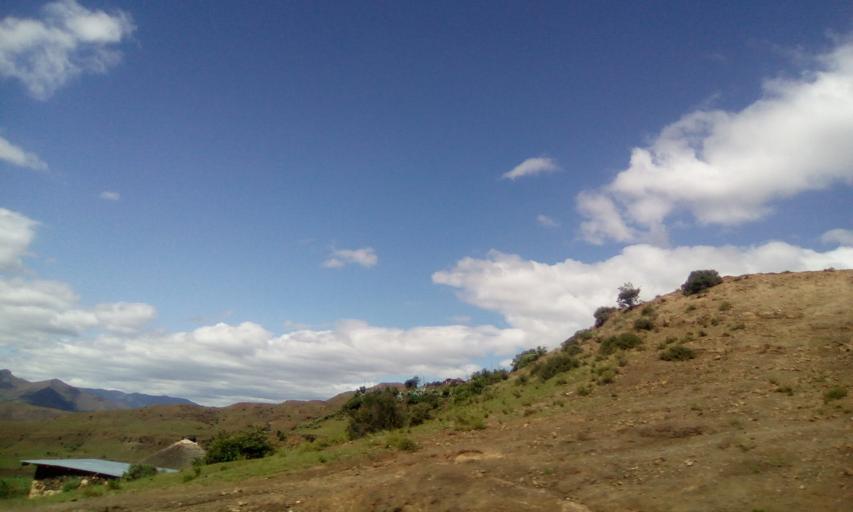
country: LS
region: Maseru
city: Nako
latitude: -29.6635
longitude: 27.7928
